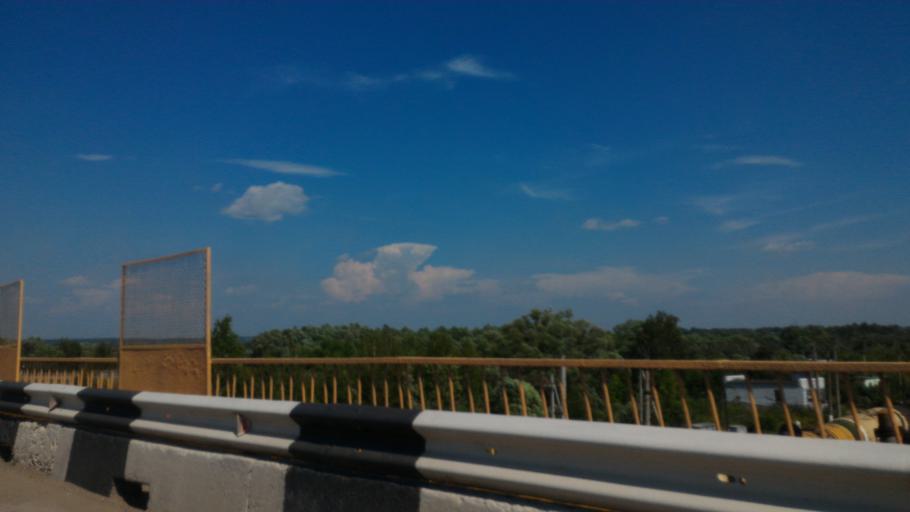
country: RU
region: Rjazan
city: Rybnoye
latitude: 54.7398
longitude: 39.4842
